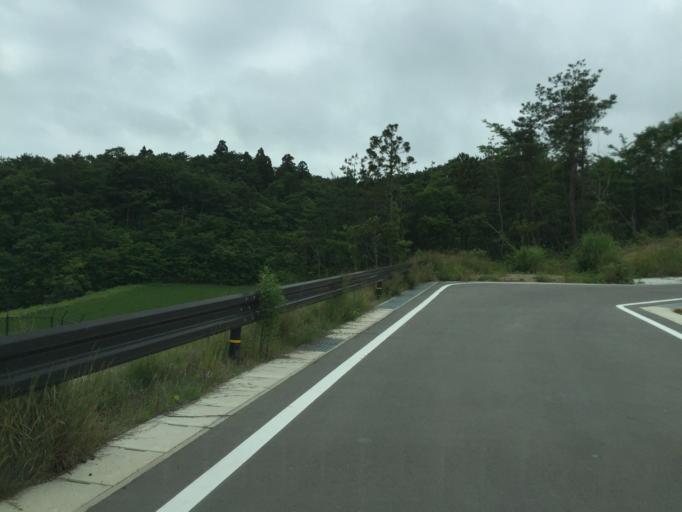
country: JP
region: Miyagi
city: Marumori
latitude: 37.7648
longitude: 140.9751
